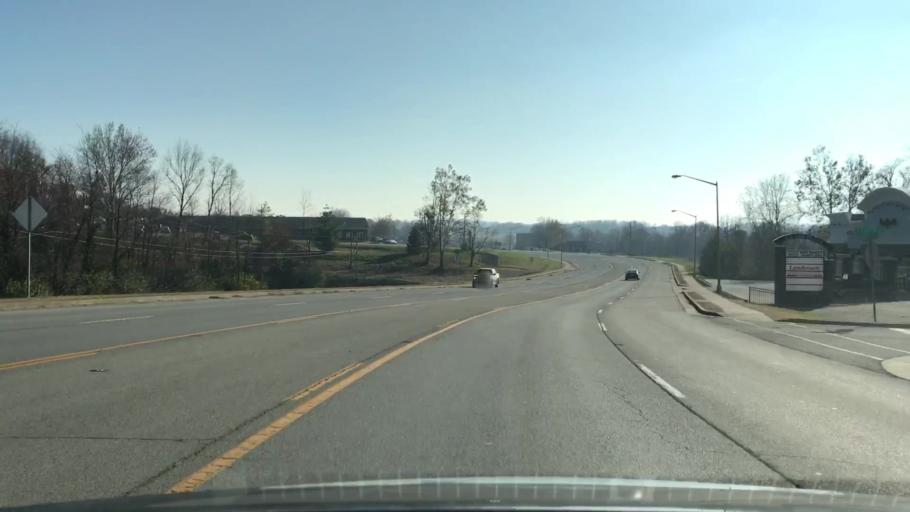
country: US
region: Kentucky
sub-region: Grayson County
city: Leitchfield
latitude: 37.4720
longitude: -86.2929
